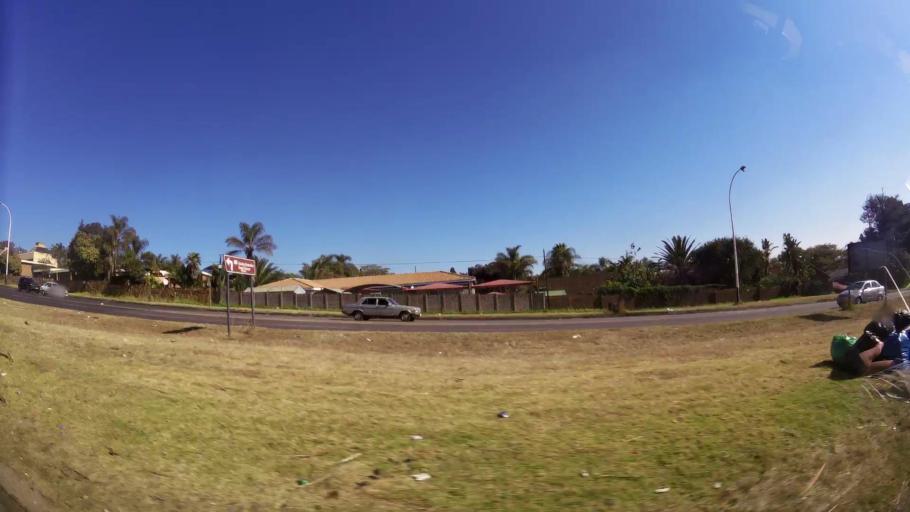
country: ZA
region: Mpumalanga
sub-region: Nkangala District Municipality
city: Witbank
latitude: -25.8670
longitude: 29.2416
